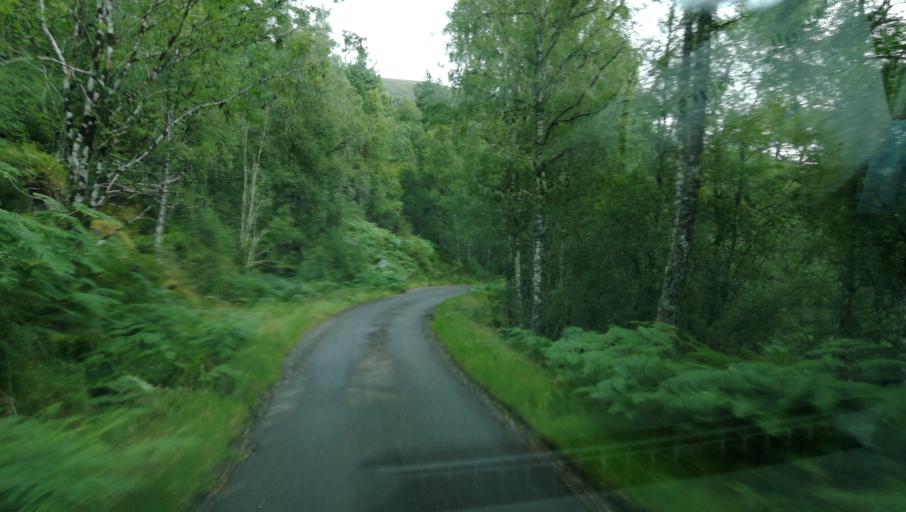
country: GB
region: Scotland
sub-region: Highland
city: Spean Bridge
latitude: 57.3097
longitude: -4.8652
